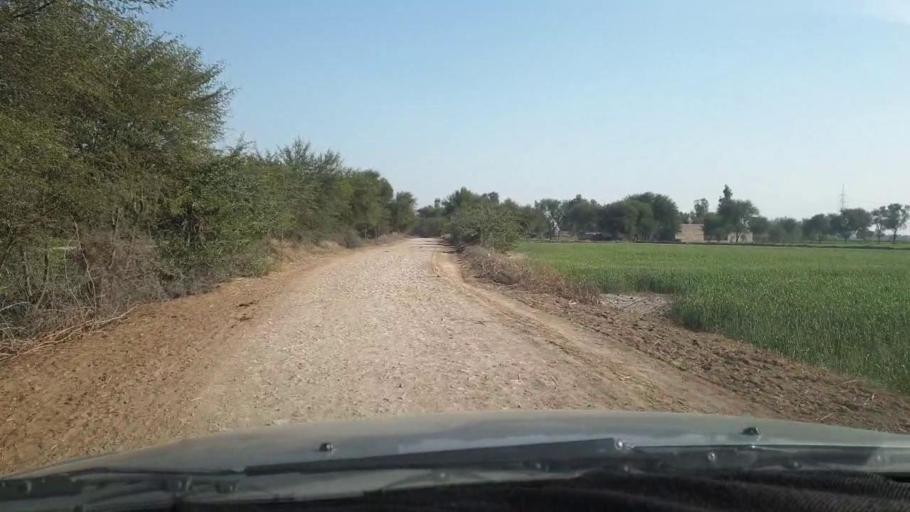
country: PK
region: Sindh
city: Mirpur Mathelo
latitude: 27.9768
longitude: 69.5476
